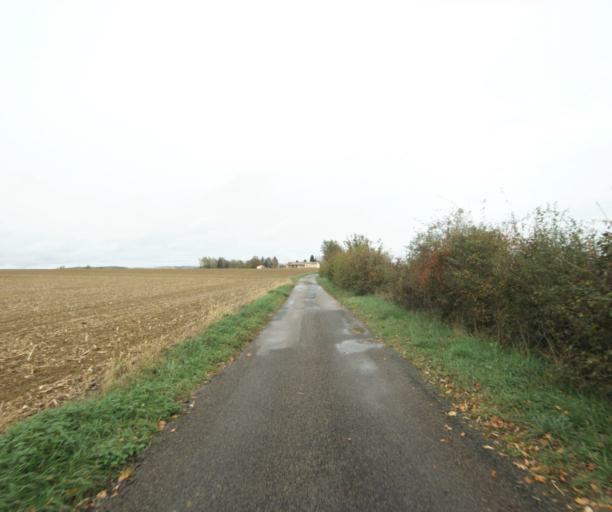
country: FR
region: Rhone-Alpes
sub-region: Departement de l'Ain
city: Pont-de-Vaux
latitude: 46.4686
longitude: 4.8728
